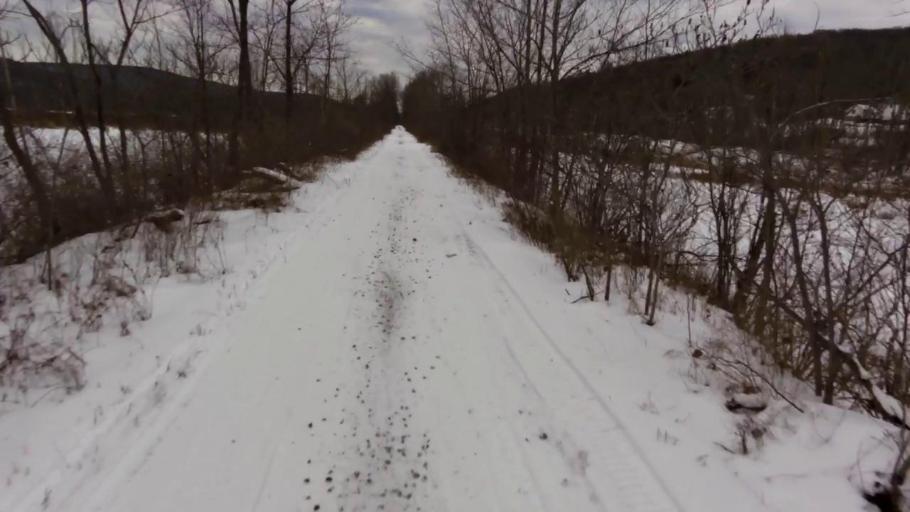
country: US
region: Pennsylvania
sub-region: McKean County
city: Foster Brook
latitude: 42.0065
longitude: -78.6238
